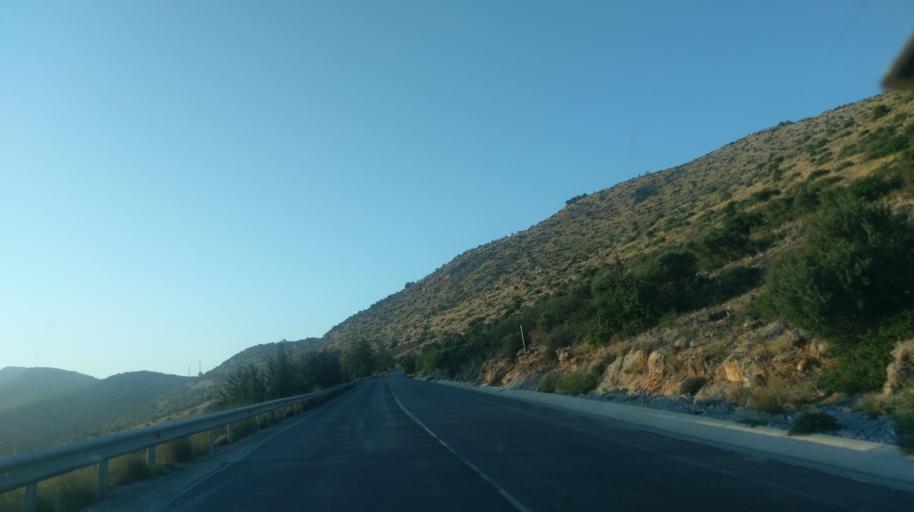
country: CY
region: Lefkosia
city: Nicosia
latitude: 35.2748
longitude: 33.4813
